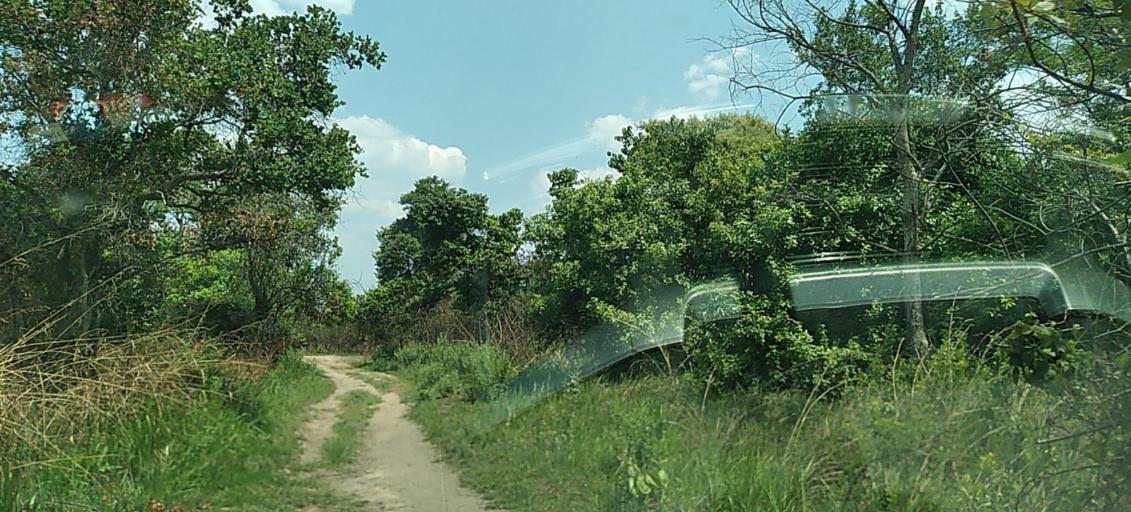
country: CD
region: Katanga
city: Kipushi
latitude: -11.9951
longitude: 27.4183
